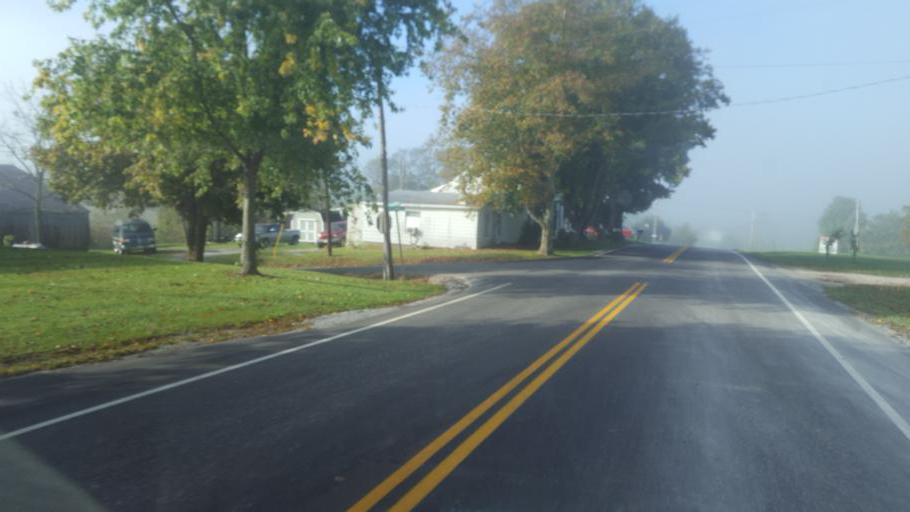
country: US
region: Kentucky
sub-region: Fleming County
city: Flemingsburg
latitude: 38.4838
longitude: -83.6382
